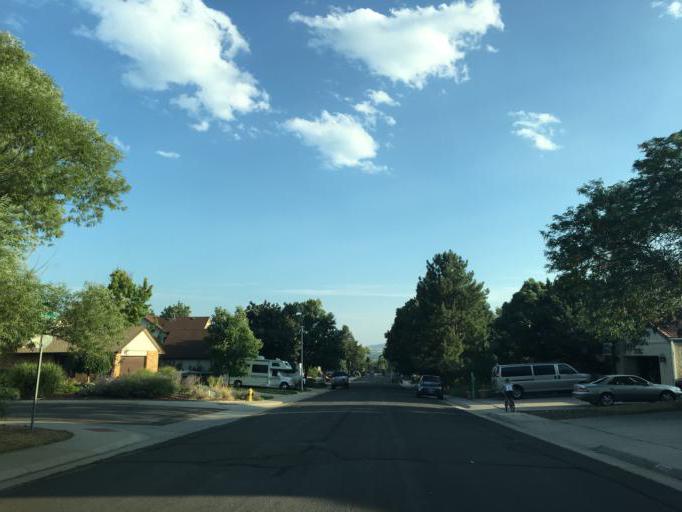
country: US
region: Colorado
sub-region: Jefferson County
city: Applewood
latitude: 39.7939
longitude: -105.1539
